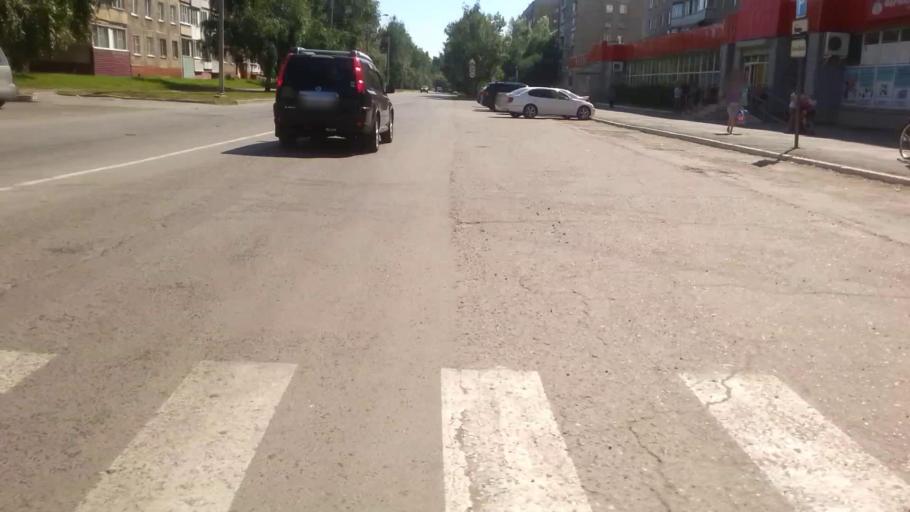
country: RU
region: Altai Krai
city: Novosilikatnyy
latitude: 53.3657
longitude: 83.6680
